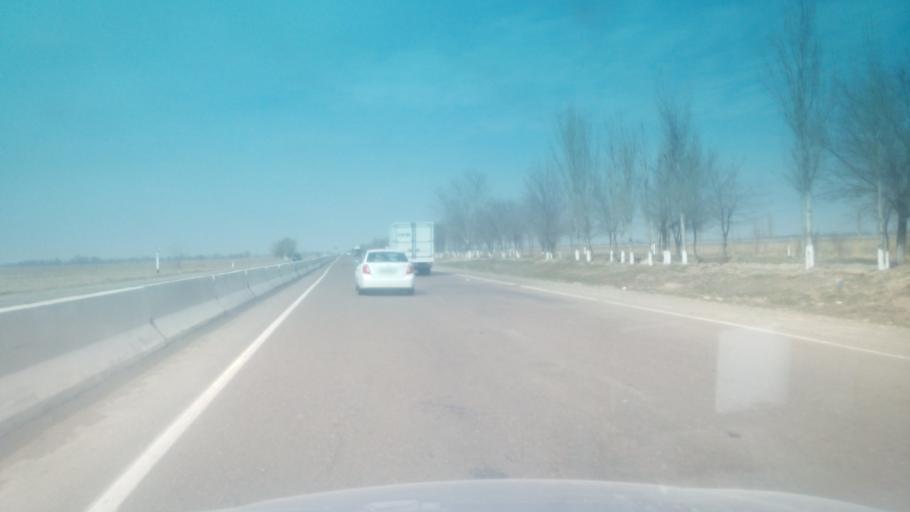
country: KZ
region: Ongtustik Qazaqstan
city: Myrzakent
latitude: 40.5262
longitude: 68.4468
